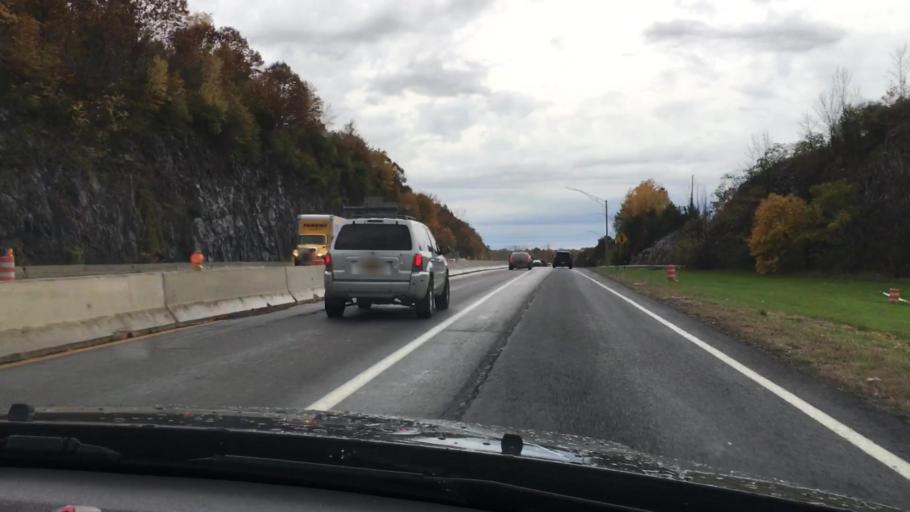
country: US
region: New York
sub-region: Orange County
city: Balmville
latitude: 41.5196
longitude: -74.0240
